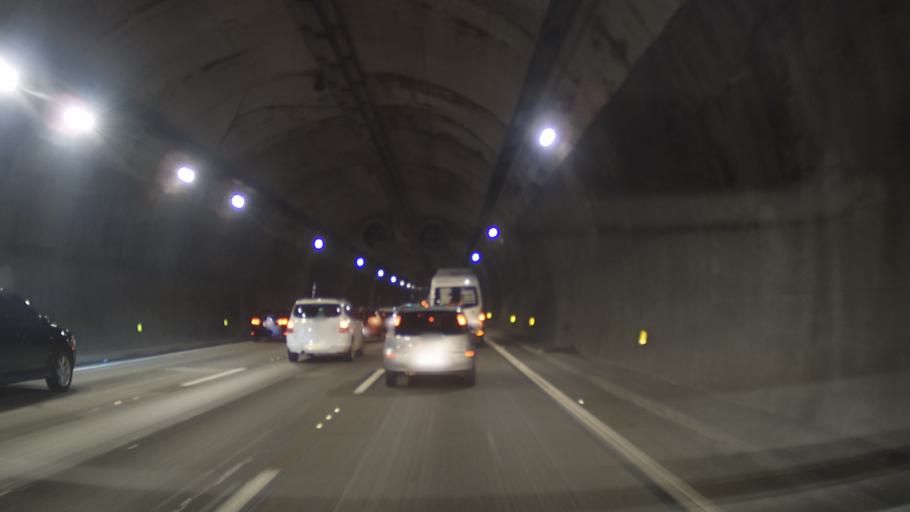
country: BR
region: Sao Paulo
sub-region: Cubatao
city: Cubatao
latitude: -23.8834
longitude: -46.4960
